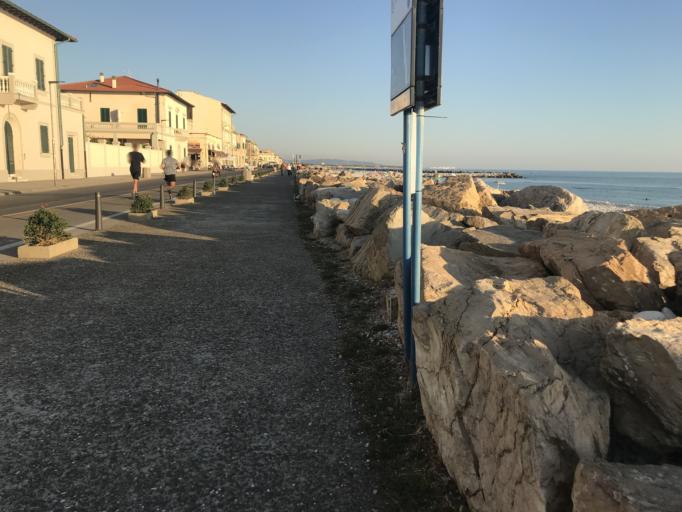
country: IT
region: Tuscany
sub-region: Province of Pisa
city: Marina di Pisa
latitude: 43.6663
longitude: 10.2758
